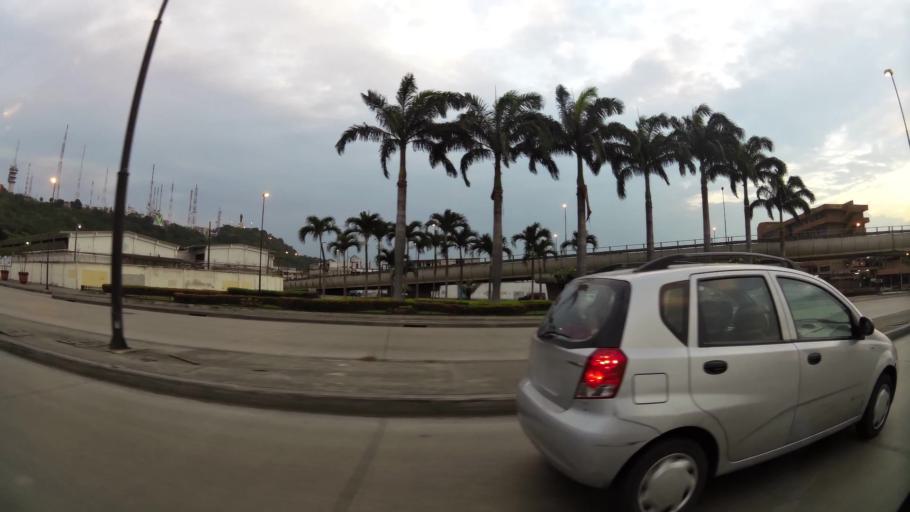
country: EC
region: Guayas
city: Eloy Alfaro
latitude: -2.1746
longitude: -79.8791
